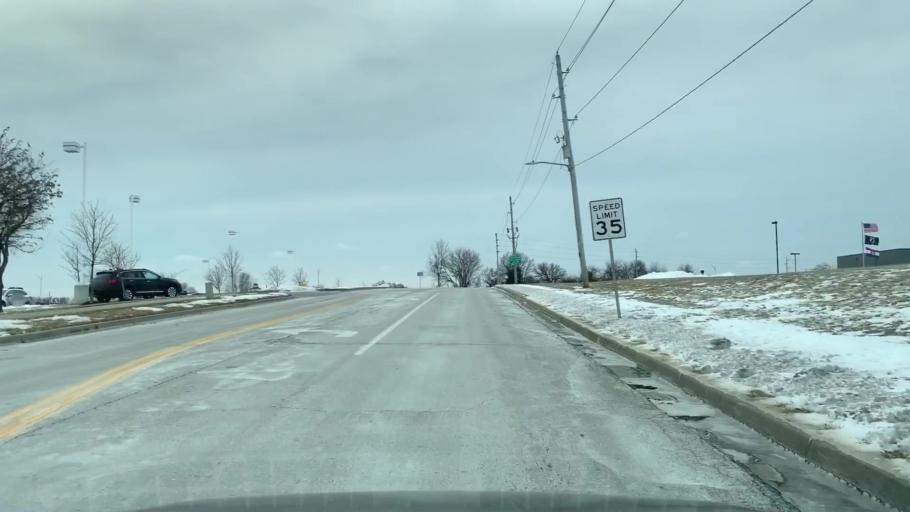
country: US
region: Missouri
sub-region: Jackson County
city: Lees Summit
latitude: 38.9494
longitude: -94.3642
